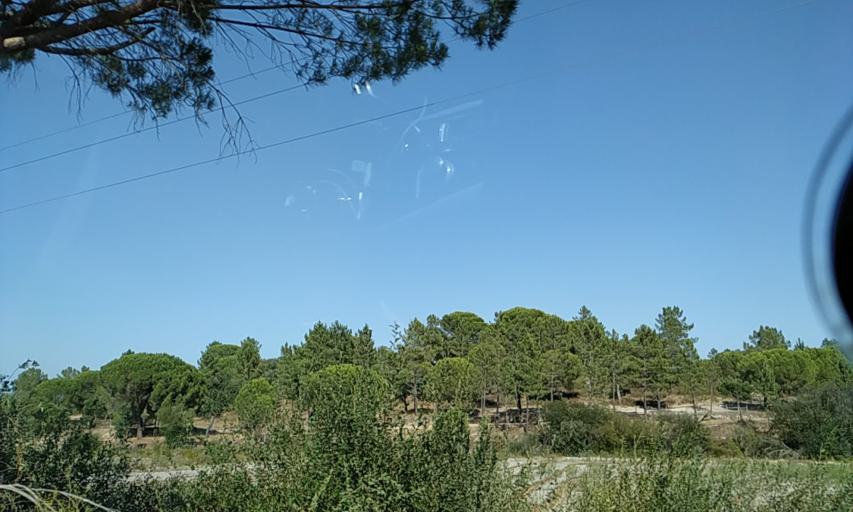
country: PT
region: Evora
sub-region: Vendas Novas
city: Vendas Novas
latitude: 38.7944
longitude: -8.5786
